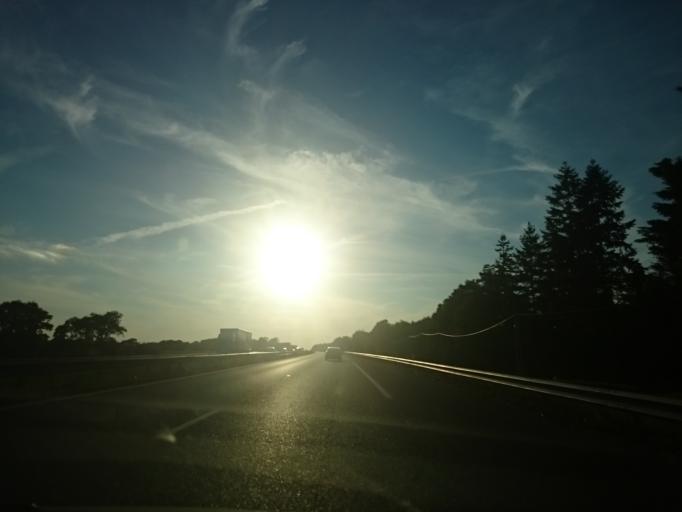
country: FR
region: Brittany
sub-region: Departement du Morbihan
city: Ploeren
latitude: 47.6614
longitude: -2.8292
